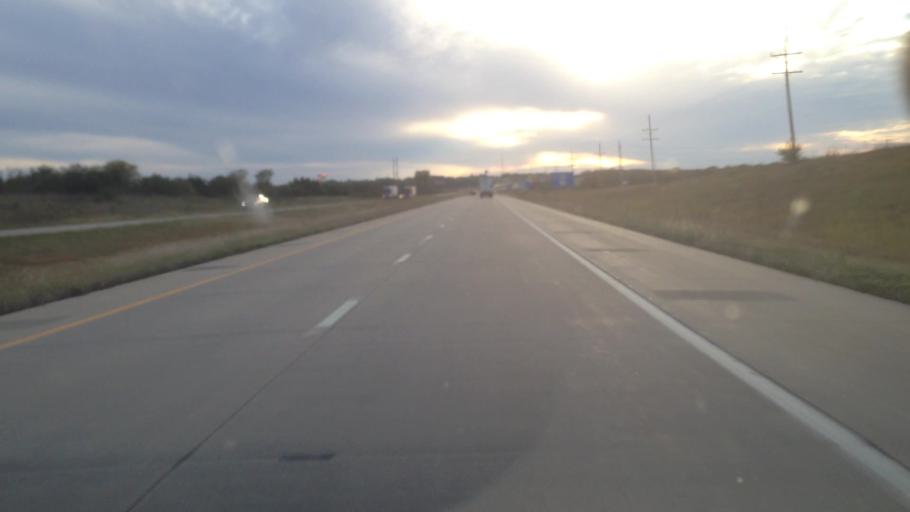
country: US
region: Kansas
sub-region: Franklin County
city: Ottawa
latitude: 38.5814
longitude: -95.2511
